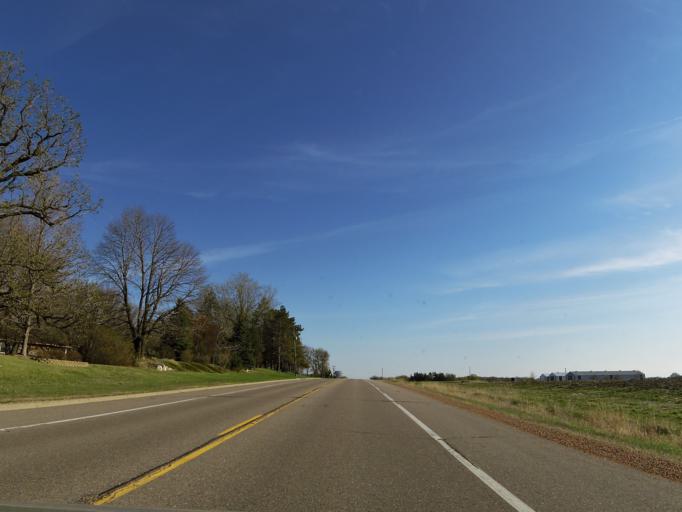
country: US
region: Minnesota
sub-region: Scott County
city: Prior Lake
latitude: 44.7242
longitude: -93.4902
